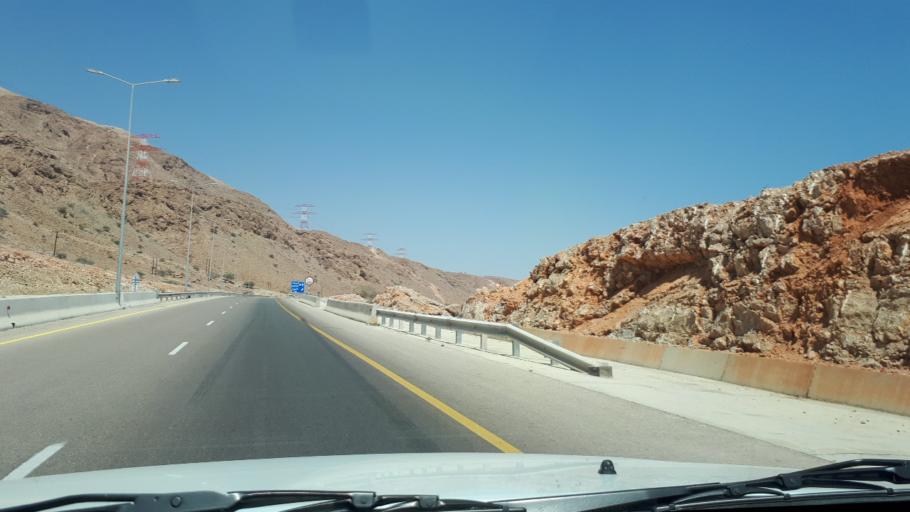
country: OM
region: Ash Sharqiyah
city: Sur
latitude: 22.8244
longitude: 59.2572
